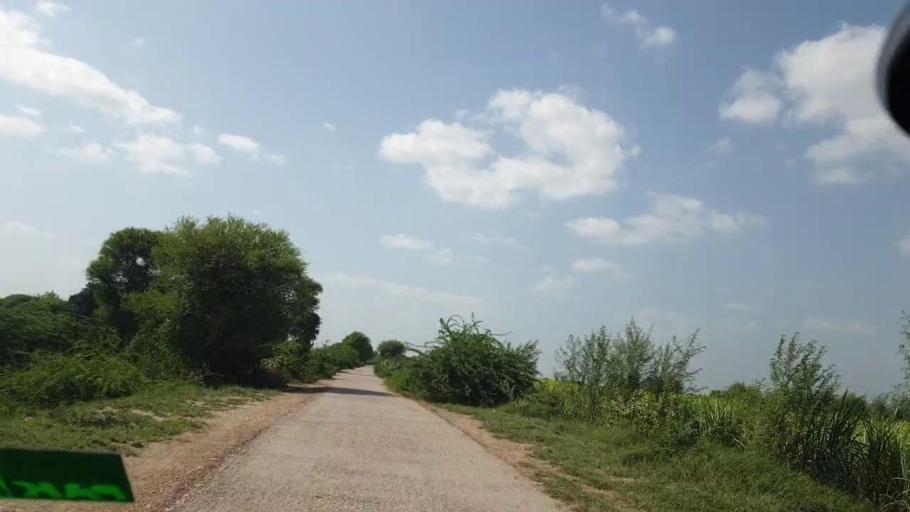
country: PK
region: Sindh
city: Naukot
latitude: 24.6530
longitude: 69.2157
